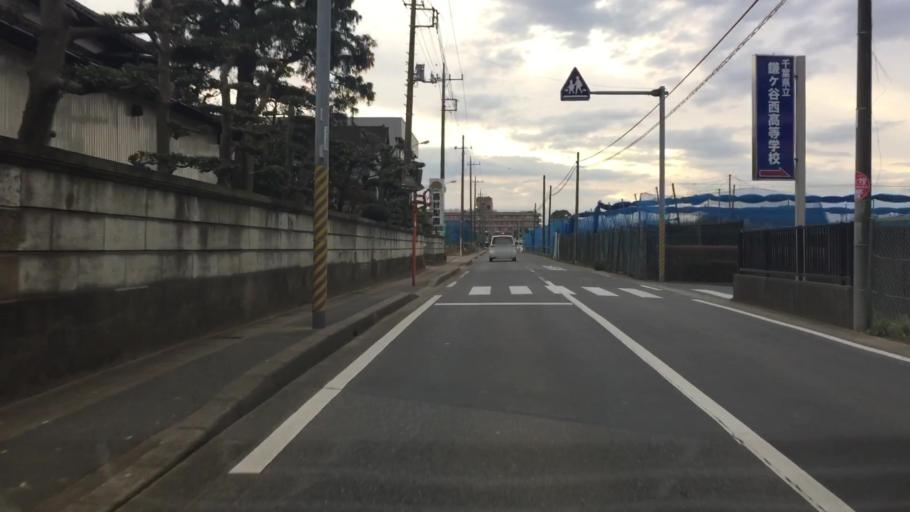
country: JP
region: Chiba
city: Kashiwa
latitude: 35.7885
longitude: 139.9903
